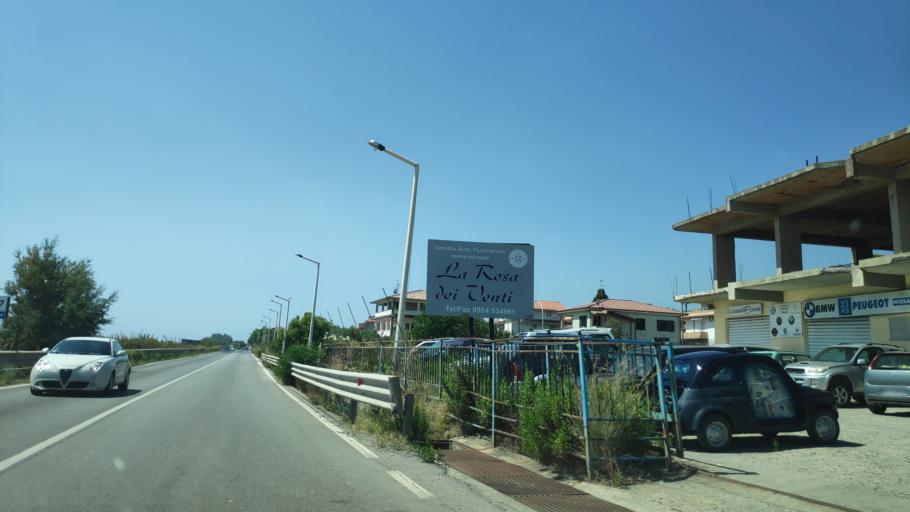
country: IT
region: Calabria
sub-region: Provincia di Reggio Calabria
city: Brancaleone-Marina
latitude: 37.9909
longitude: 16.1203
